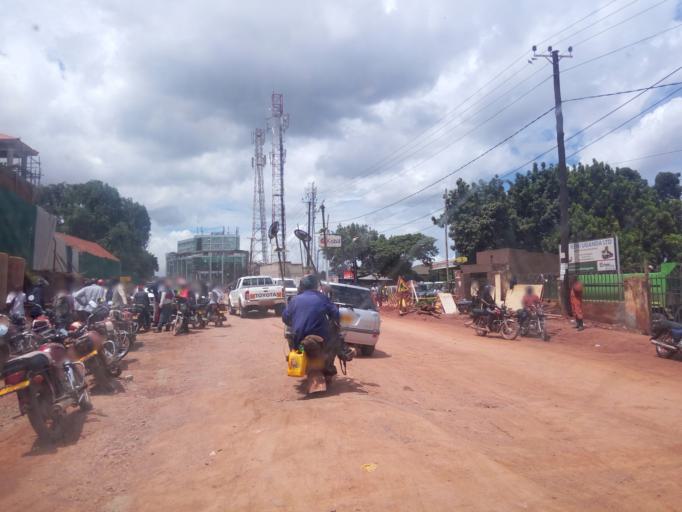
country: UG
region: Central Region
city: Kampala Central Division
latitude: 0.3280
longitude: 32.5692
